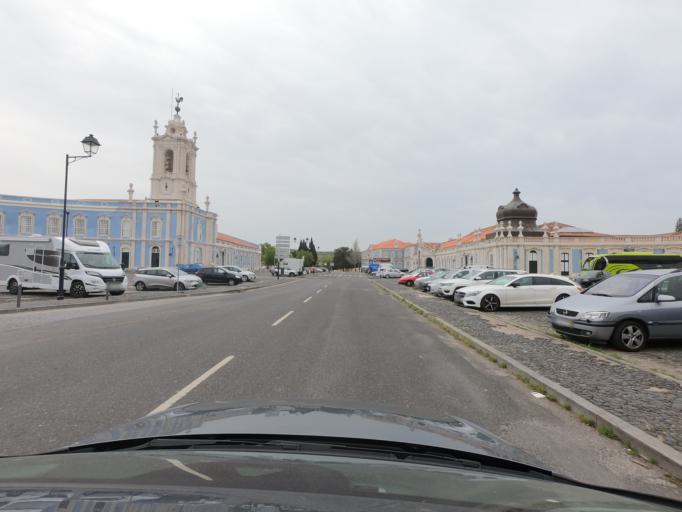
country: PT
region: Lisbon
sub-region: Sintra
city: Queluz
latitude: 38.7513
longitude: -9.2584
